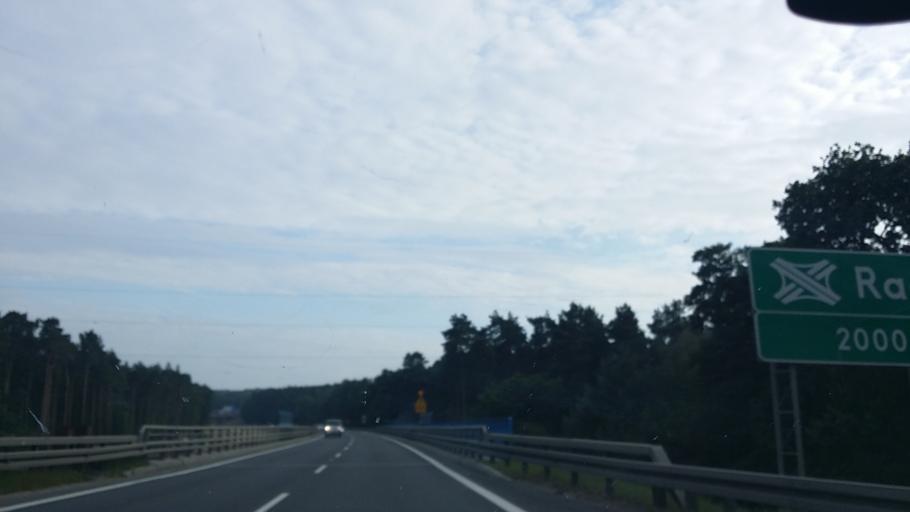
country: PL
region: Lubusz
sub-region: Zielona Gora
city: Zielona Gora
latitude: 51.9454
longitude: 15.5486
